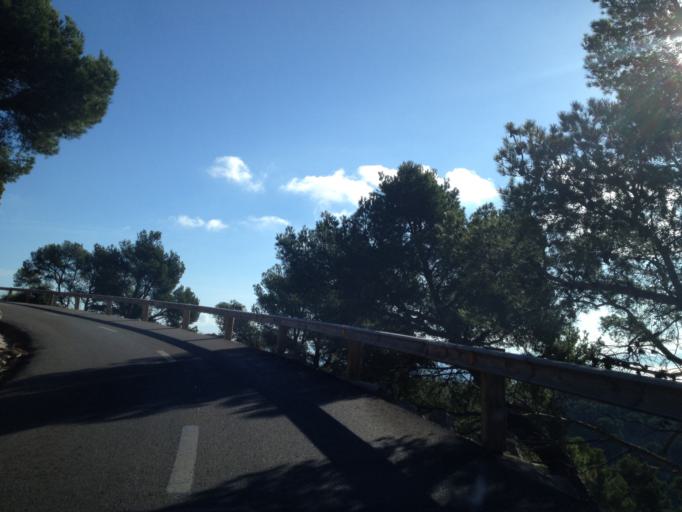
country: ES
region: Balearic Islands
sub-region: Illes Balears
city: Alcudia
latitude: 39.9508
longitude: 3.1950
